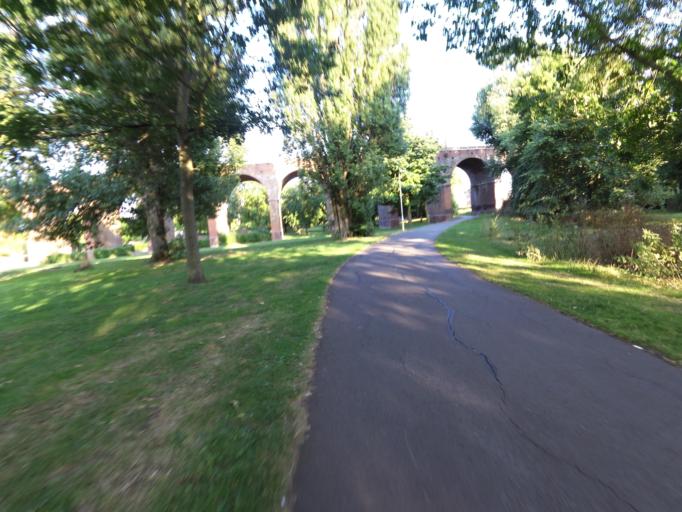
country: GB
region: England
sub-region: Essex
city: Chelmsford
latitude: 51.7328
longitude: 0.4623
